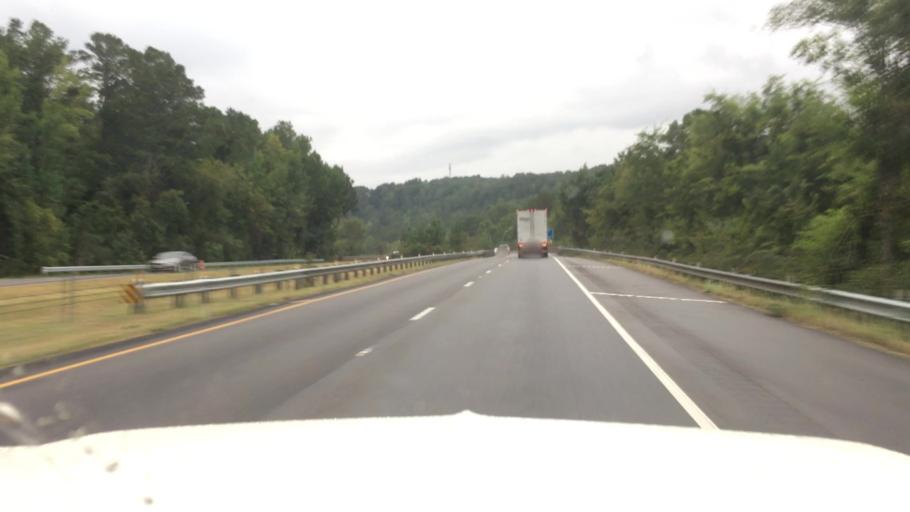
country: US
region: Alabama
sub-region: Morgan County
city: Falkville
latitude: 34.3317
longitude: -86.8988
